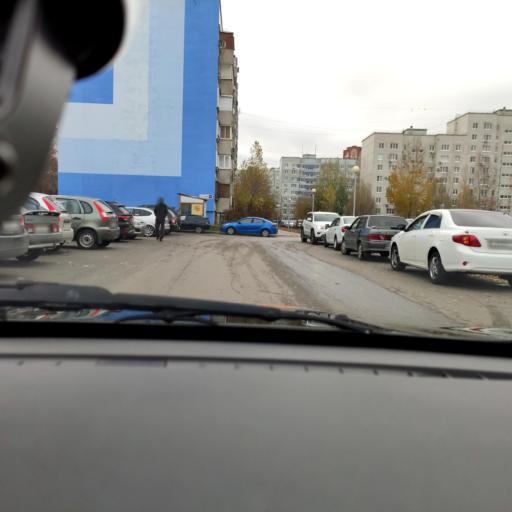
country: RU
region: Samara
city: Tol'yatti
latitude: 53.5477
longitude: 49.3356
